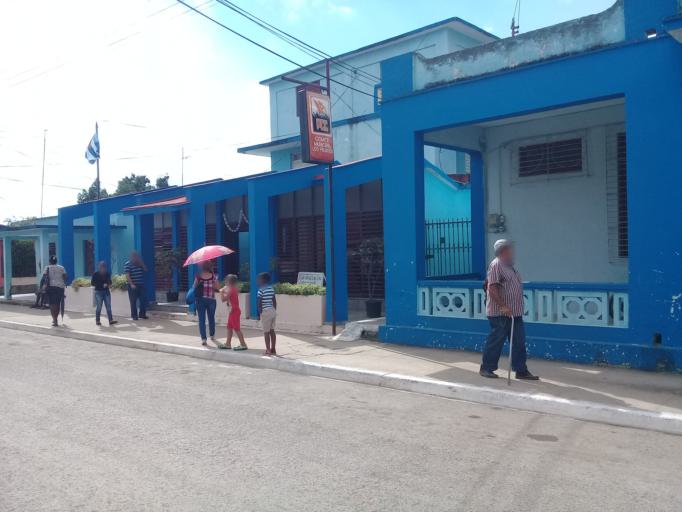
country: CU
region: Pinar del Rio
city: Los Palacios
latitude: 22.5859
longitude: -83.2504
